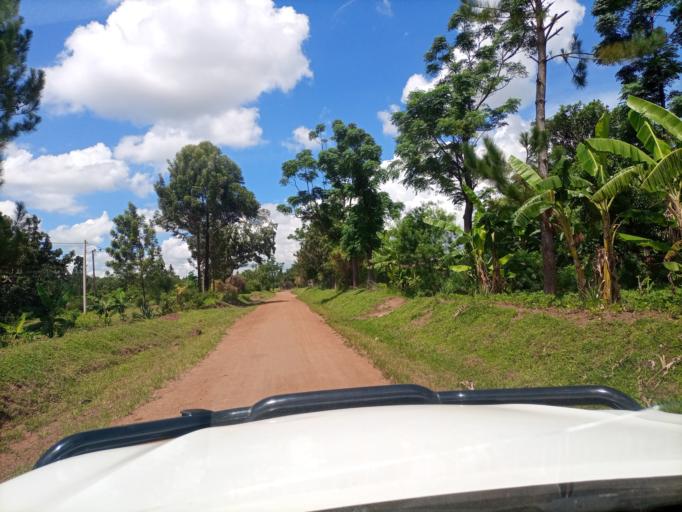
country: UG
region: Eastern Region
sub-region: Tororo District
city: Tororo
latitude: 0.7009
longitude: 34.0131
